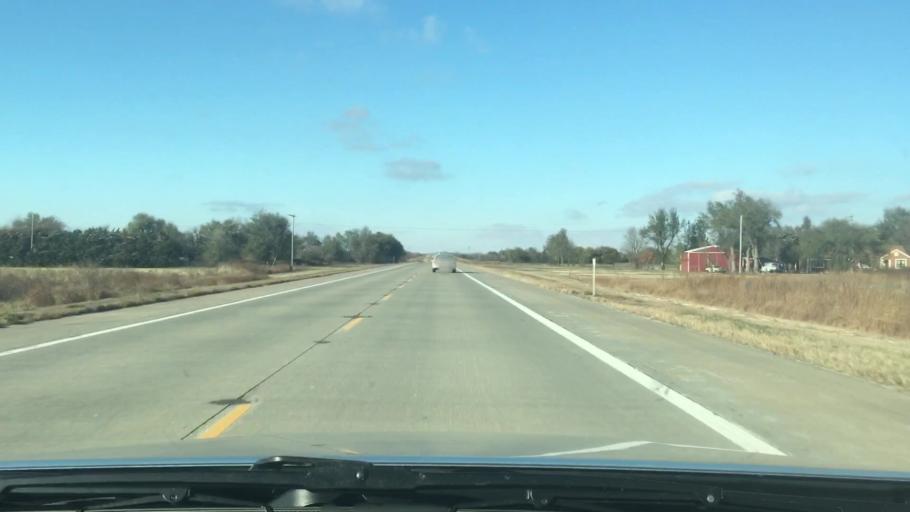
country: US
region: Kansas
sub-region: Reno County
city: Hutchinson
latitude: 38.0703
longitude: -97.9870
